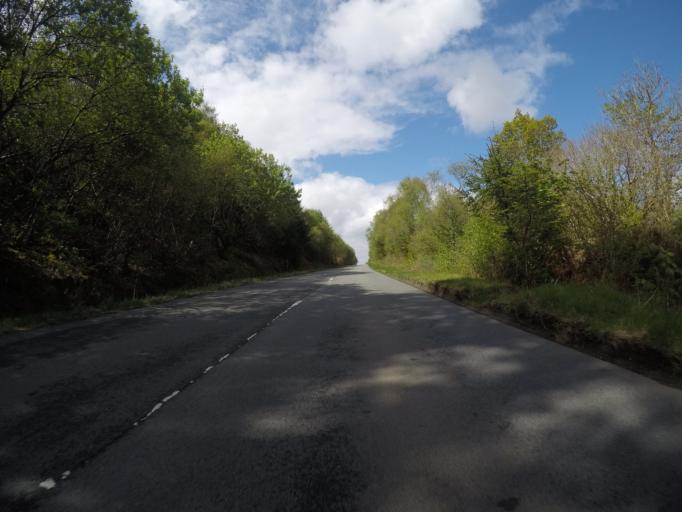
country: GB
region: Scotland
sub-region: Highland
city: Isle of Skye
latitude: 57.4592
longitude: -6.3285
